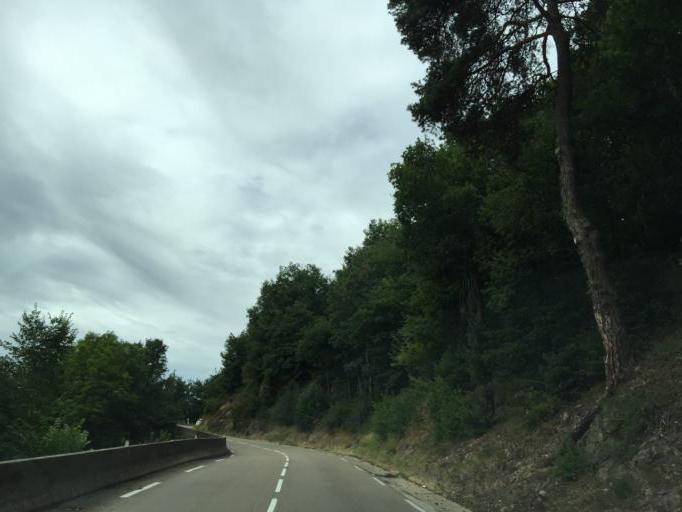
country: FR
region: Rhone-Alpes
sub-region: Departement de la Loire
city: Saint-Paul-en-Cornillon
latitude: 45.4070
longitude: 4.2257
